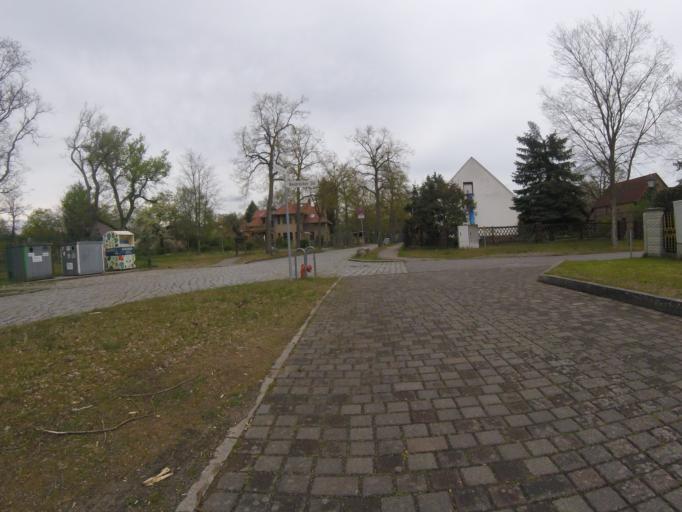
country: DE
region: Brandenburg
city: Bestensee
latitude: 52.2250
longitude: 13.6555
